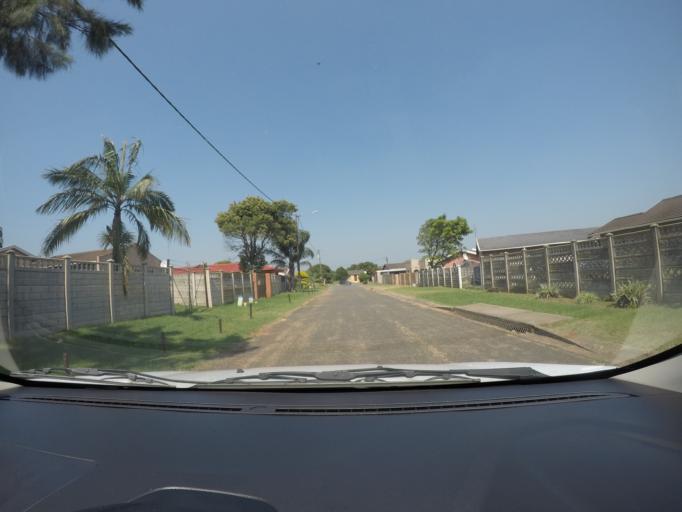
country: ZA
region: KwaZulu-Natal
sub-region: uThungulu District Municipality
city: eSikhawini
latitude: -28.8666
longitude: 31.9157
